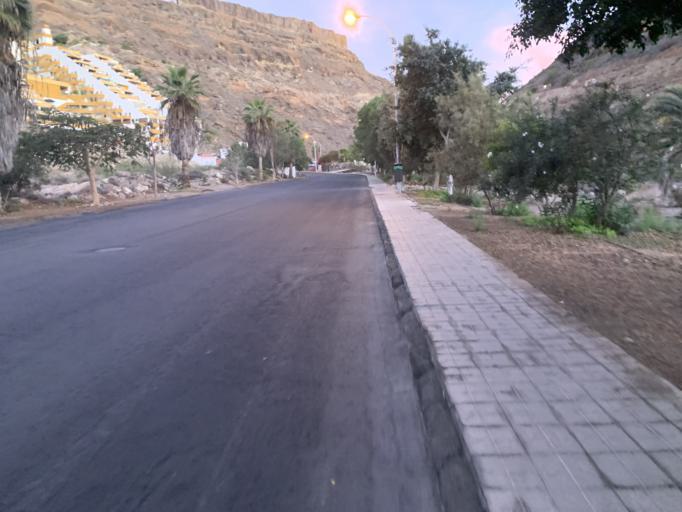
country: ES
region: Canary Islands
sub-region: Provincia de Las Palmas
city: Puerto Rico
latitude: 27.8020
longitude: -15.7318
